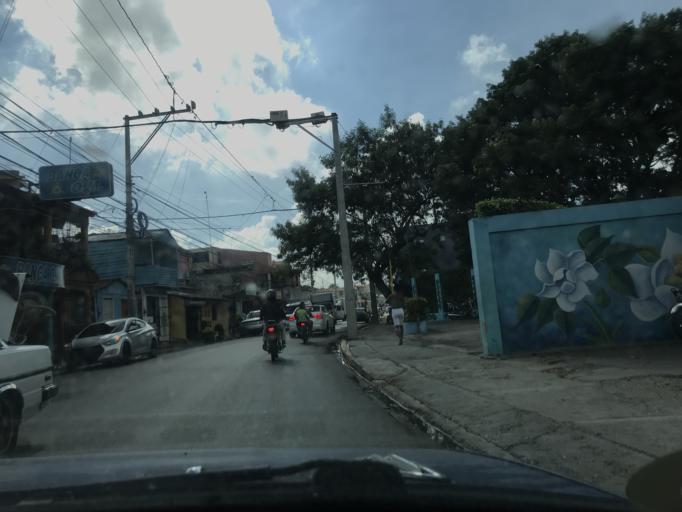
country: DO
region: Santiago
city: Santiago de los Caballeros
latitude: 19.4553
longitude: -70.7214
